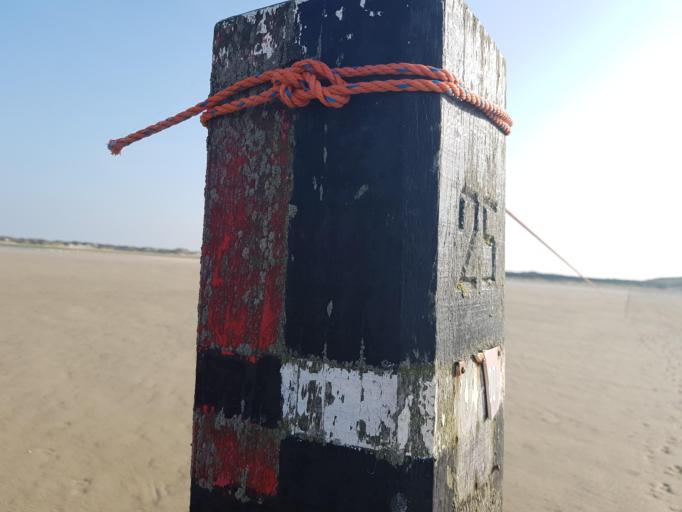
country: NL
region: North Holland
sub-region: Gemeente Texel
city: Den Burg
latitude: 53.1392
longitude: 4.8004
